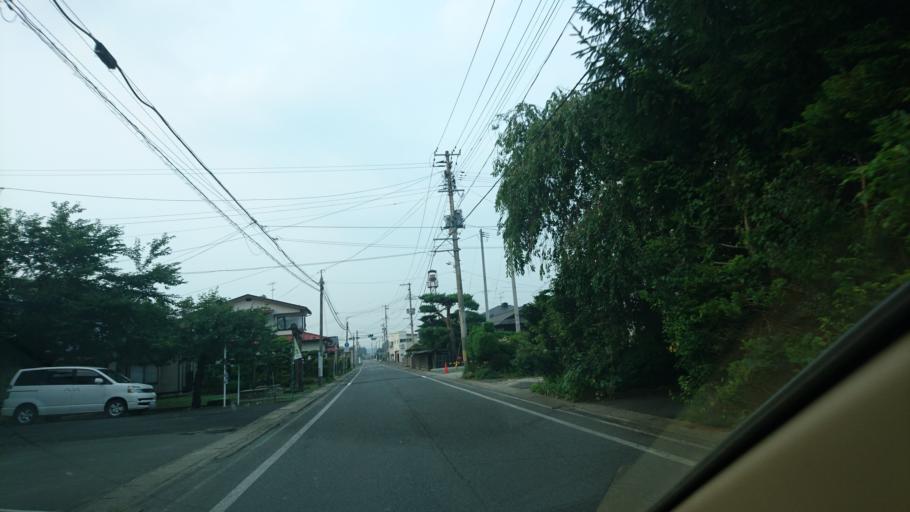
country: JP
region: Iwate
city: Mizusawa
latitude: 39.1751
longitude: 141.1551
